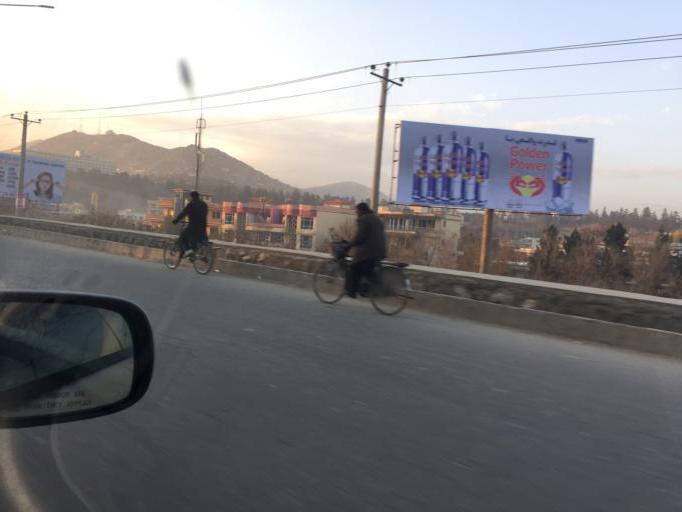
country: AF
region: Kabul
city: Kabul
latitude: 34.5348
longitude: 69.1329
